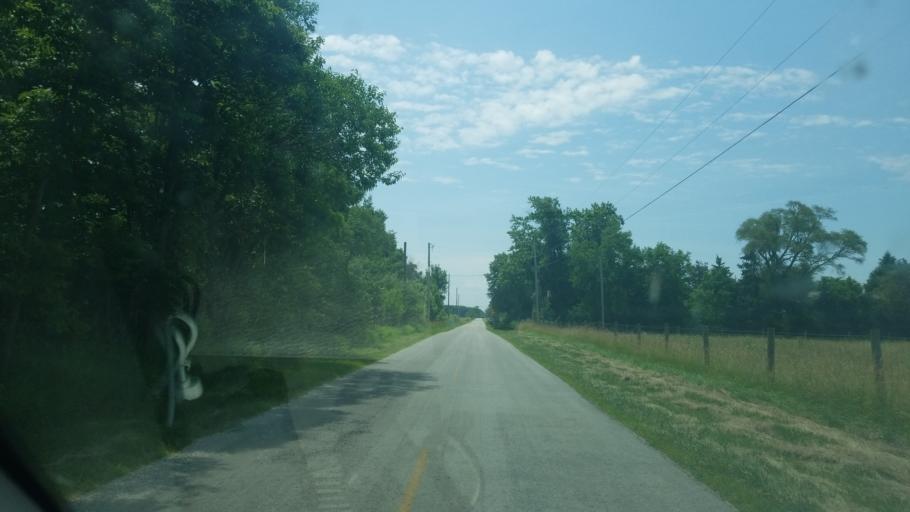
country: US
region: Ohio
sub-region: Wood County
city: North Baltimore
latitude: 41.2311
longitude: -83.6211
